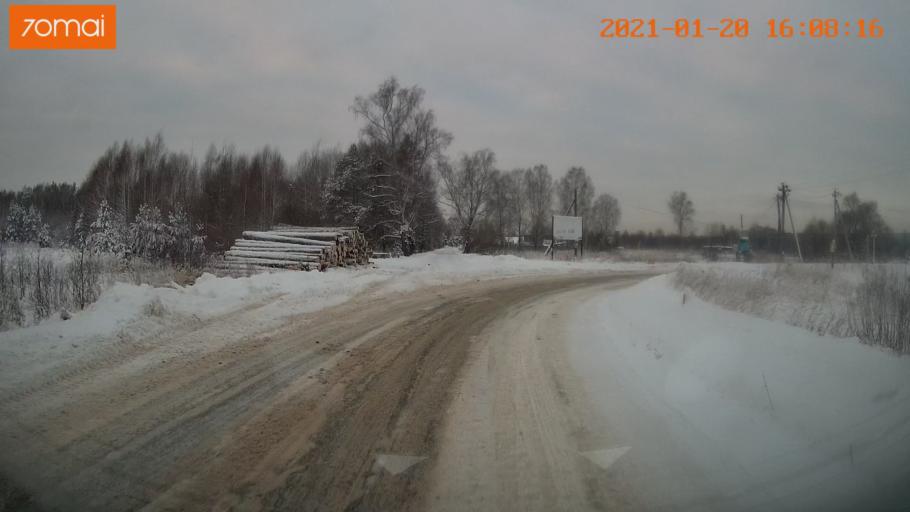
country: RU
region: Vladimir
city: Sudogda
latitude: 56.0756
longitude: 40.7680
